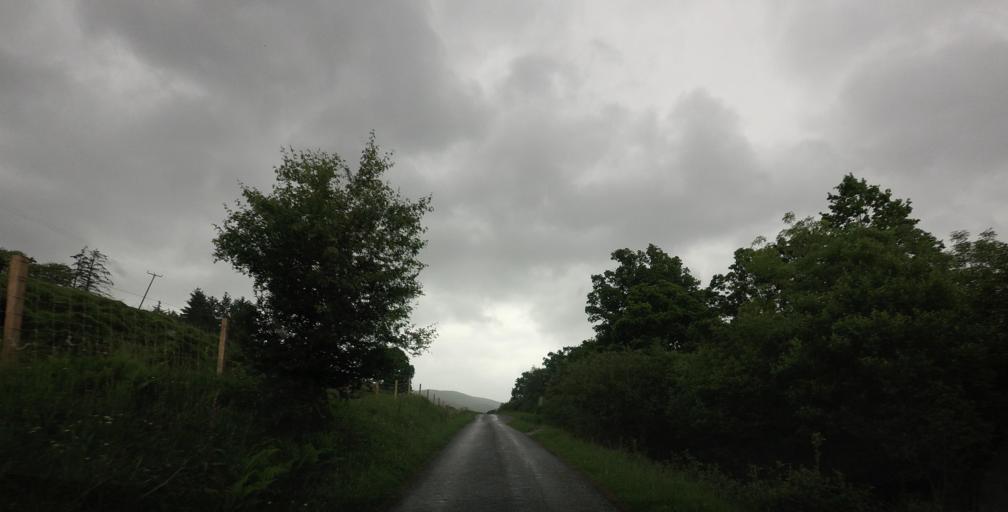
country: GB
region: Scotland
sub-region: Argyll and Bute
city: Oban
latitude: 56.7123
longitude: -5.5631
